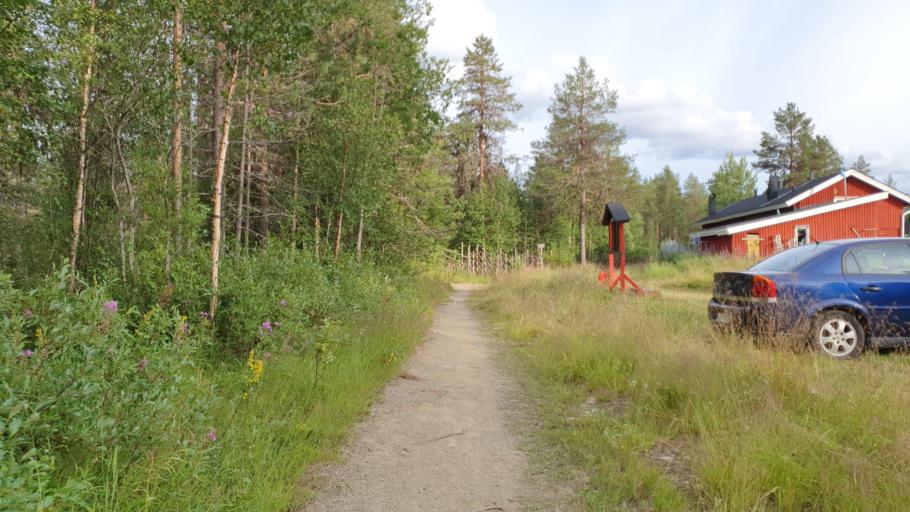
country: FI
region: Lapland
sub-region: Tunturi-Lappi
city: Kolari
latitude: 67.6260
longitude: 24.1771
